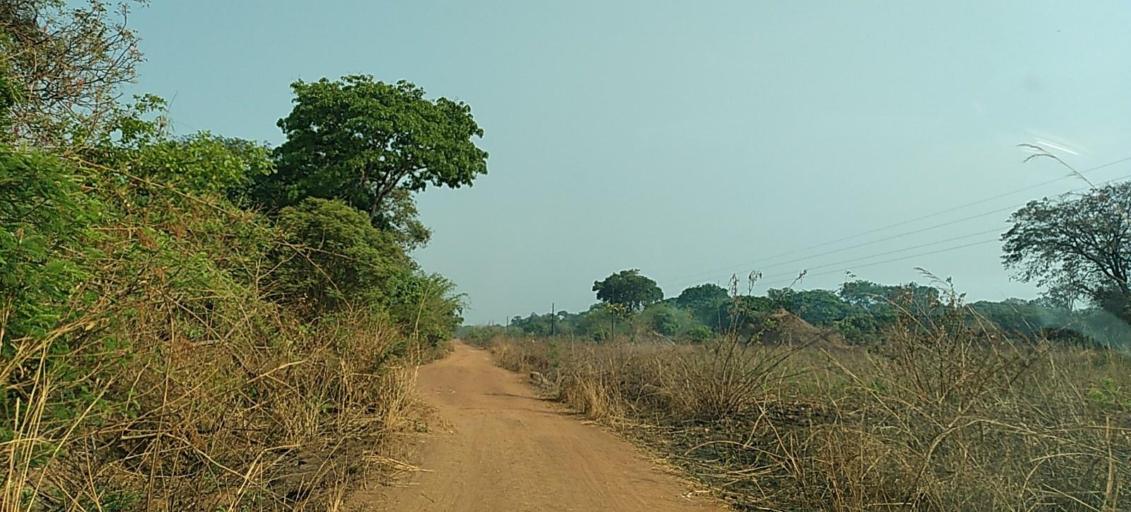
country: ZM
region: Copperbelt
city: Chingola
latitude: -12.8492
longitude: 27.5506
